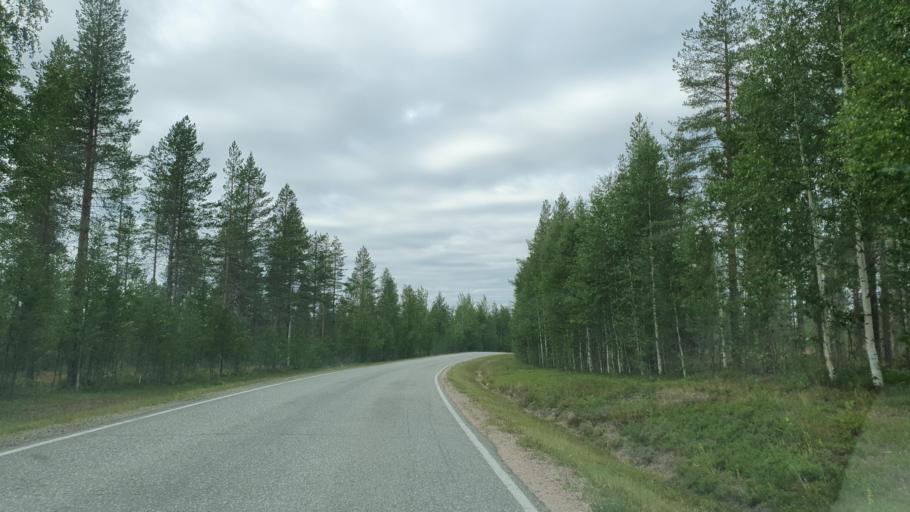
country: FI
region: Lapland
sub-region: Tunturi-Lappi
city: Kittilae
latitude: 67.6081
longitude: 25.2752
